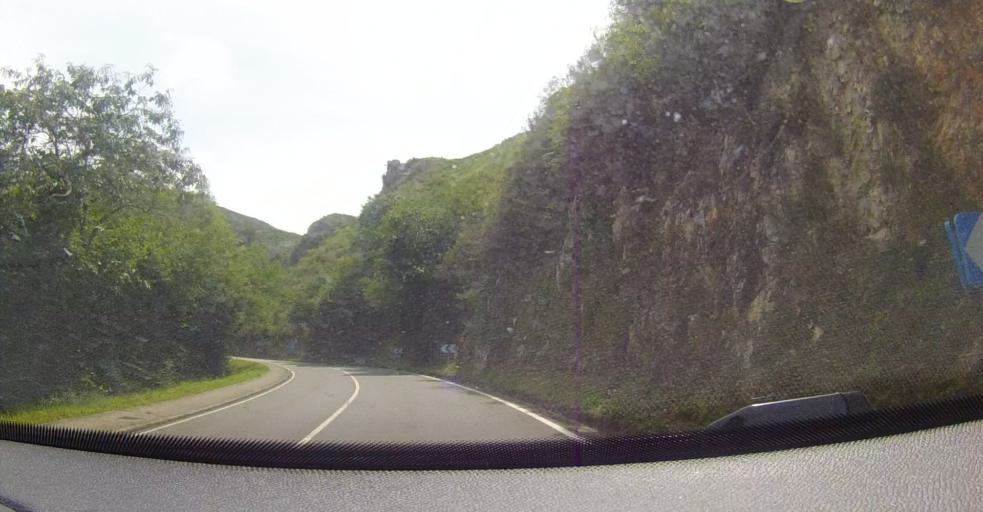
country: ES
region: Asturias
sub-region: Province of Asturias
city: Cangas de Onis
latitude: 43.3323
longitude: -5.0829
